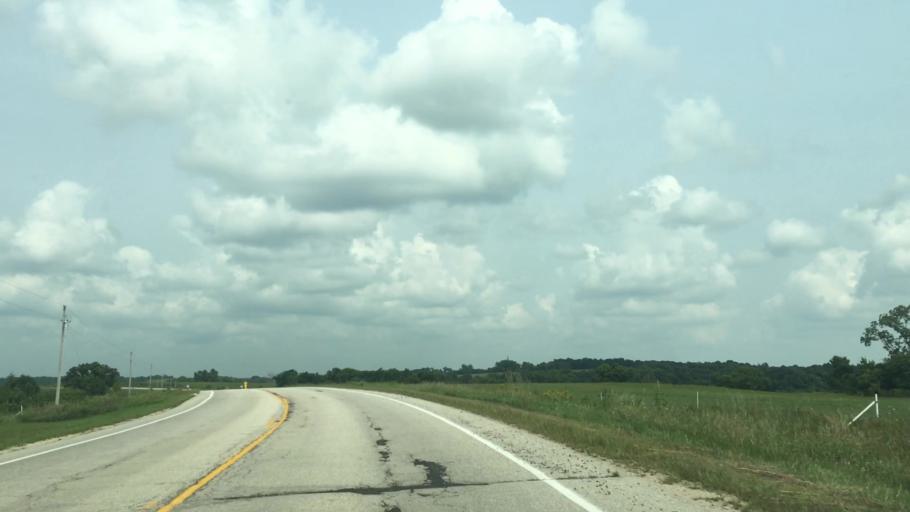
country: US
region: Minnesota
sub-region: Fillmore County
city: Preston
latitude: 43.6836
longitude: -91.9424
